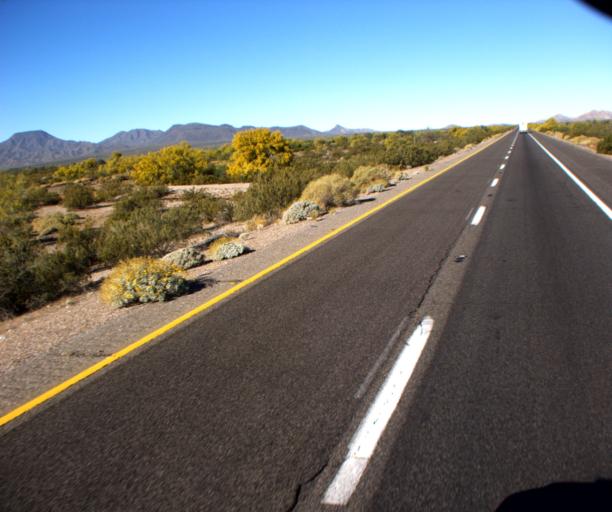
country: US
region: Arizona
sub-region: Pinal County
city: Maricopa
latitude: 32.8304
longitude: -112.0190
